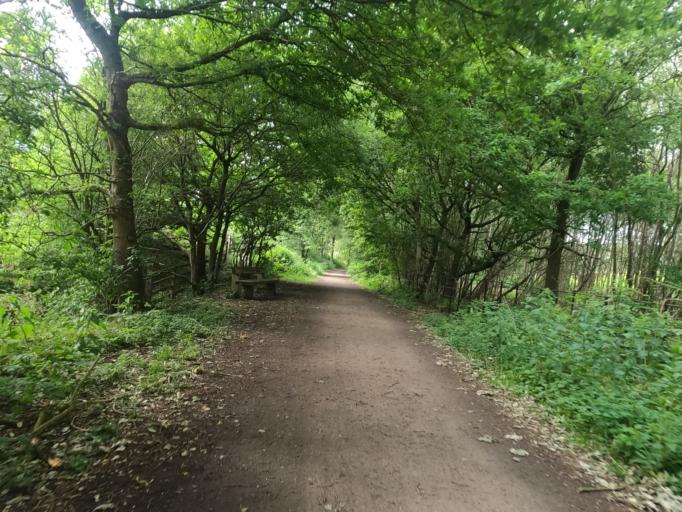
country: GB
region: England
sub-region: Cheshire West and Chester
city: Cuddington
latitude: 53.2237
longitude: -2.6179
